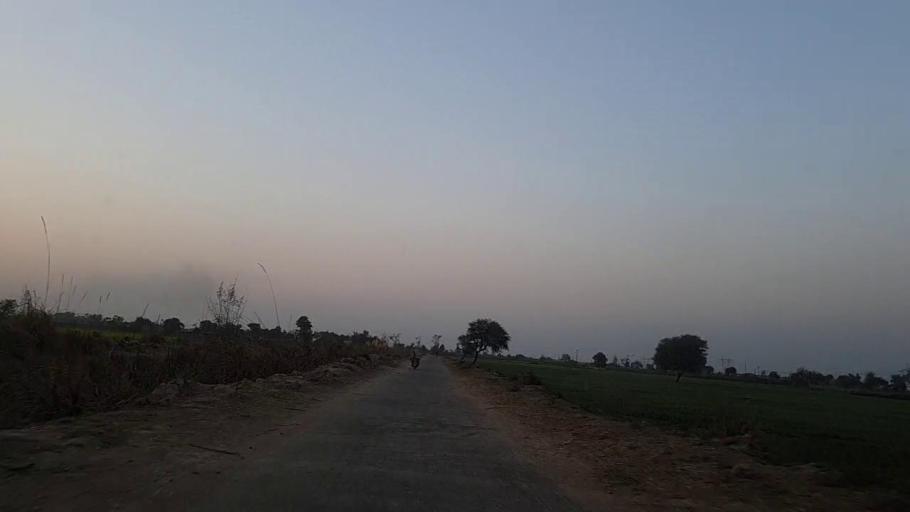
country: PK
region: Sindh
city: Hala
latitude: 25.9524
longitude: 68.4259
